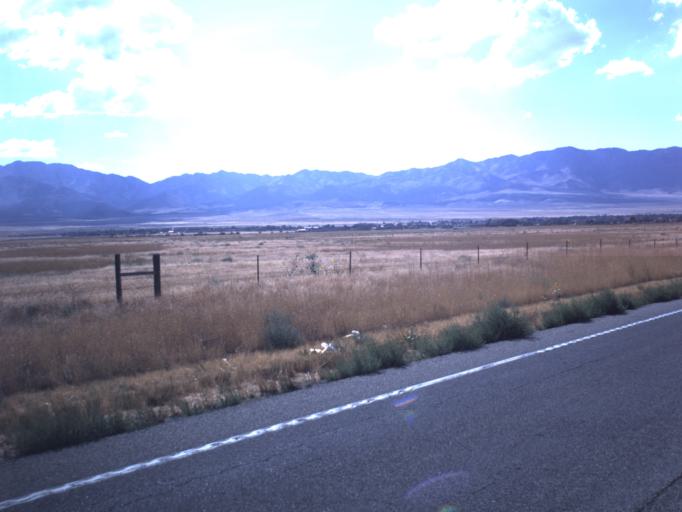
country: US
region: Utah
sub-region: Tooele County
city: Grantsville
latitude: 40.5808
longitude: -112.3987
